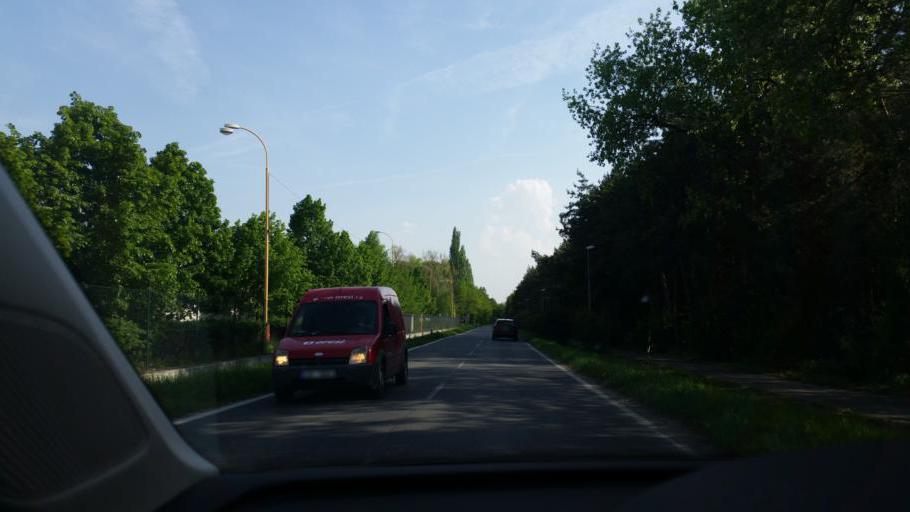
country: CZ
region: Central Bohemia
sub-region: Okres Kolin
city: Kolin
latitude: 50.0468
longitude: 15.1993
